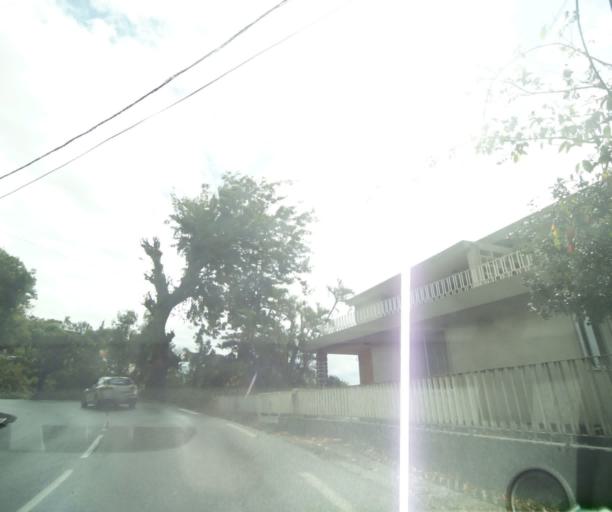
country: RE
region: Reunion
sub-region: Reunion
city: Saint-Paul
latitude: -20.9961
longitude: 55.3286
